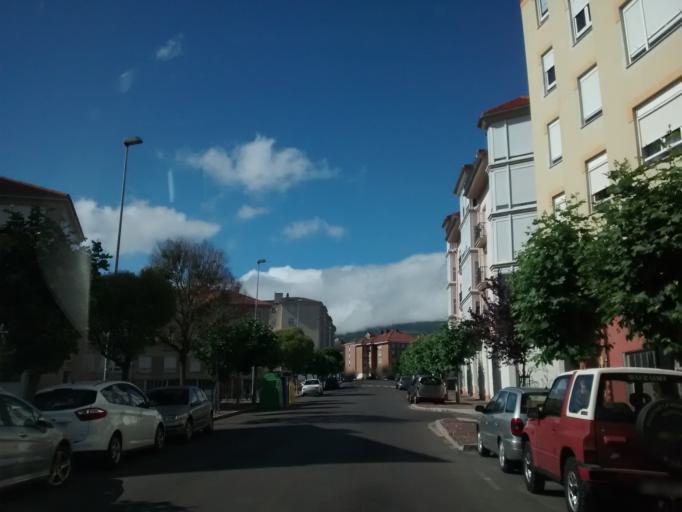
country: ES
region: Cantabria
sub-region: Provincia de Cantabria
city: Reinosa
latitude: 43.0011
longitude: -4.1404
